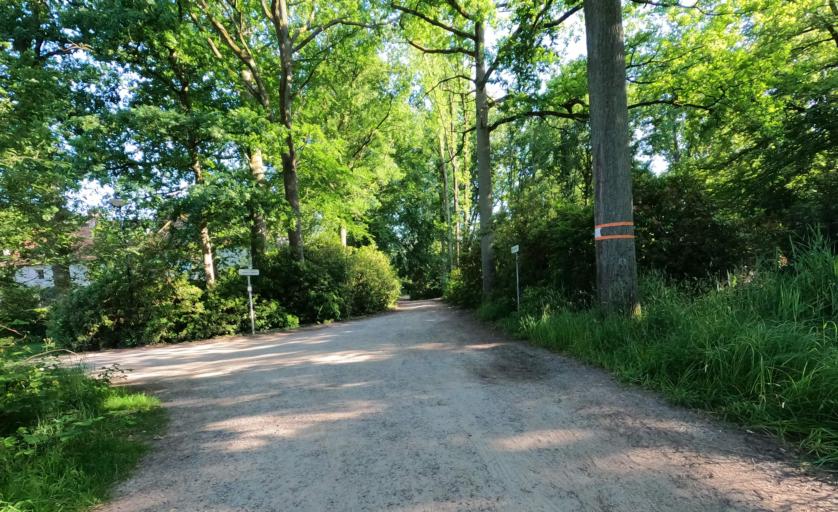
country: BE
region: Flanders
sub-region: Provincie Antwerpen
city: Schilde
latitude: 51.2558
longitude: 4.5705
